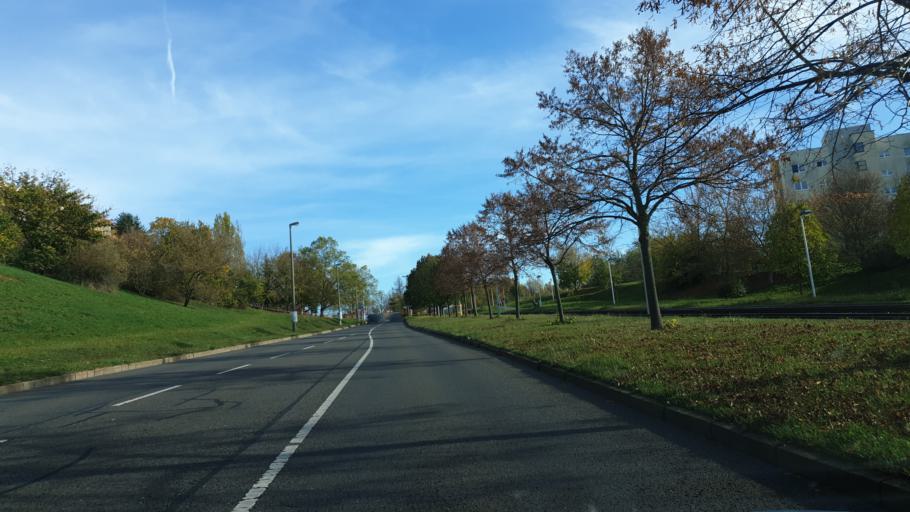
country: DE
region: Thuringia
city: Gera
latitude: 50.9017
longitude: 12.0935
